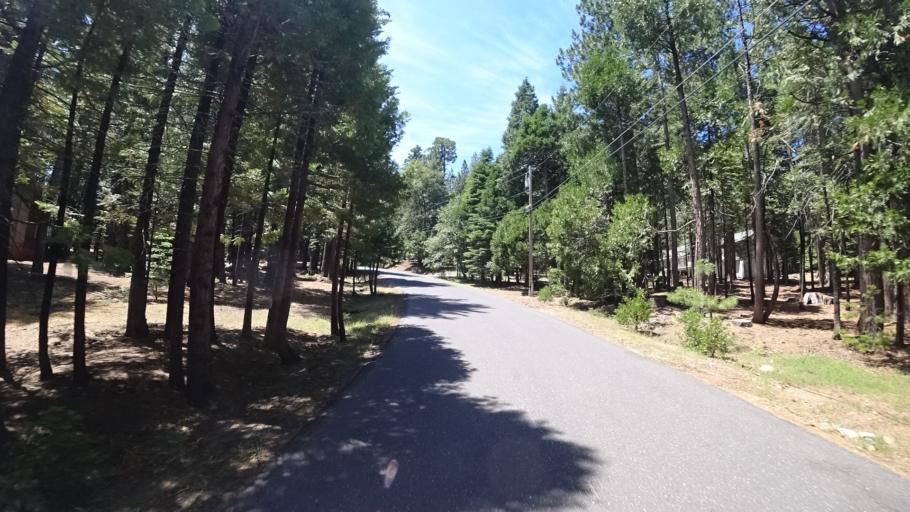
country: US
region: California
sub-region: Calaveras County
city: Arnold
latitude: 38.3088
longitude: -120.2592
